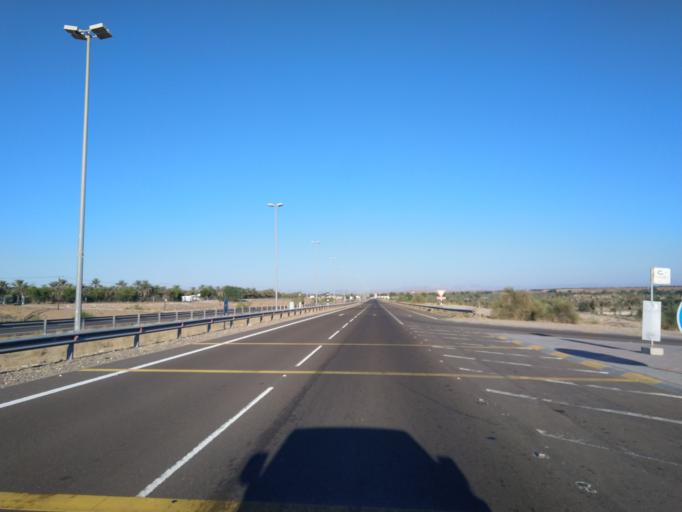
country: OM
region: Al Buraimi
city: Al Buraymi
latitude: 24.5422
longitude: 55.6439
